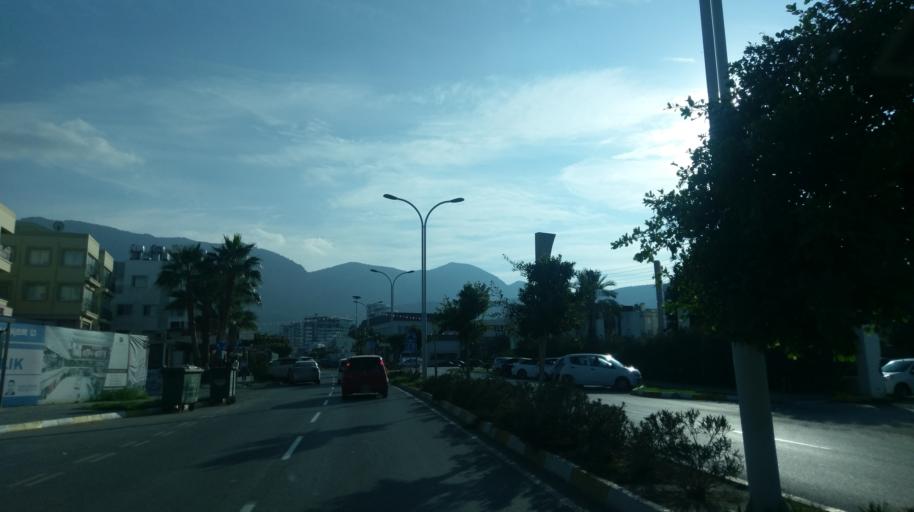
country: CY
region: Keryneia
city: Kyrenia
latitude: 35.3350
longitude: 33.3312
